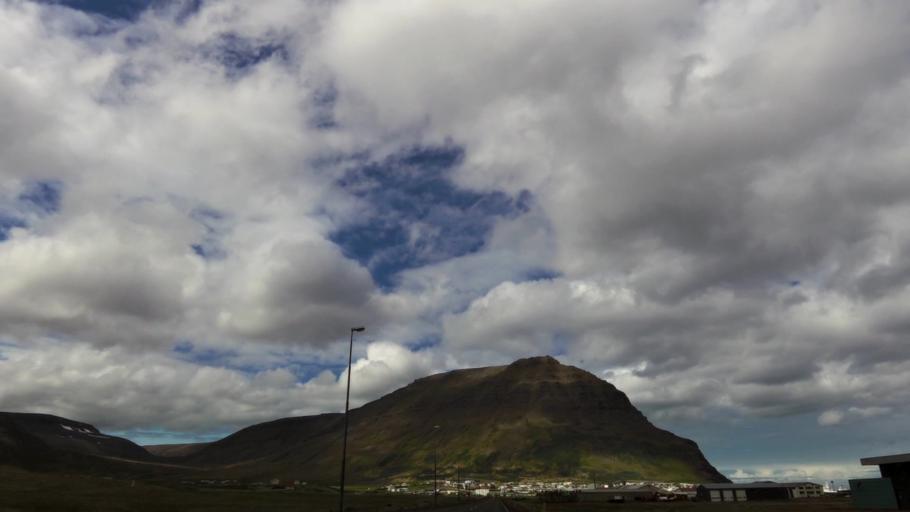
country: IS
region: Westfjords
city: Isafjoerdur
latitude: 66.1486
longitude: -23.2426
